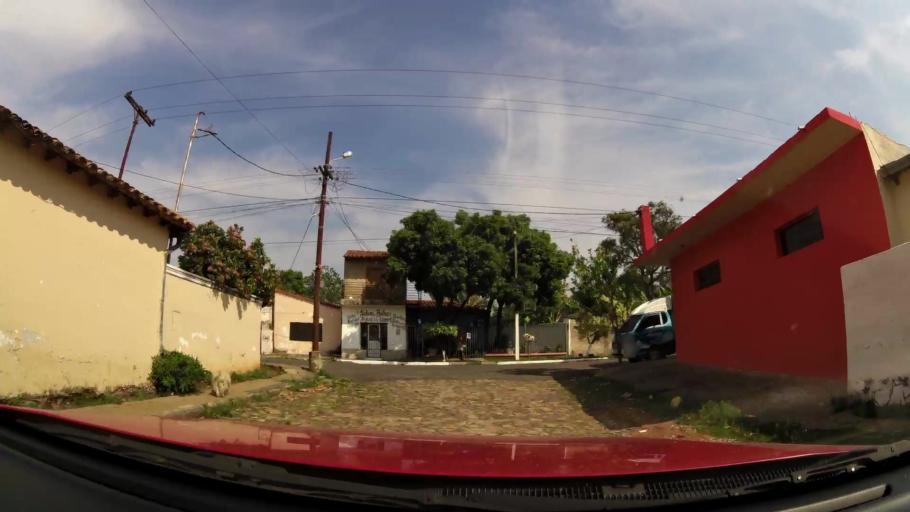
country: PY
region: Central
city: Fernando de la Mora
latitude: -25.2714
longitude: -57.5500
